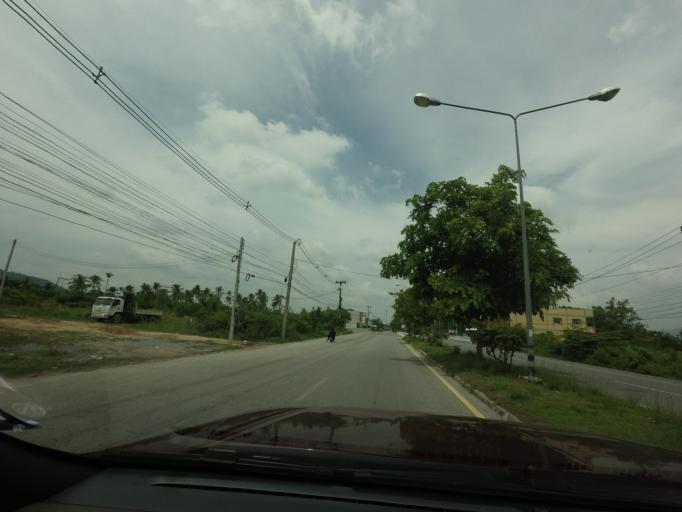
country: TH
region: Yala
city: Yala
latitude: 6.5580
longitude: 101.2980
